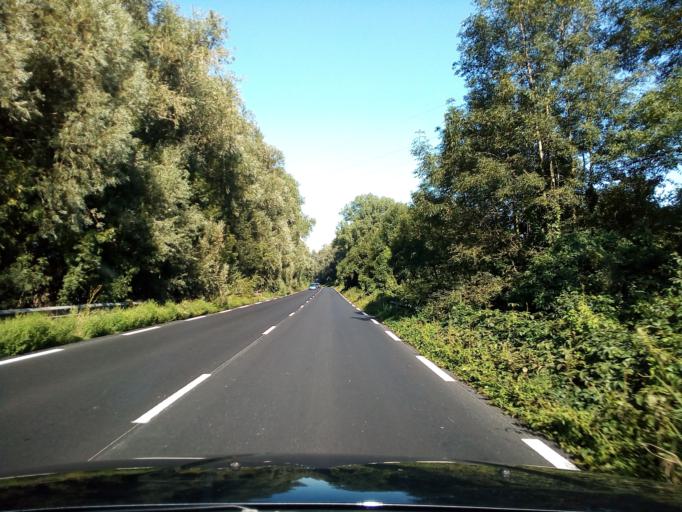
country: FR
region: Rhone-Alpes
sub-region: Departement du Rhone
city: Decines-Charpieu
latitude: 45.7820
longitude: 4.9496
